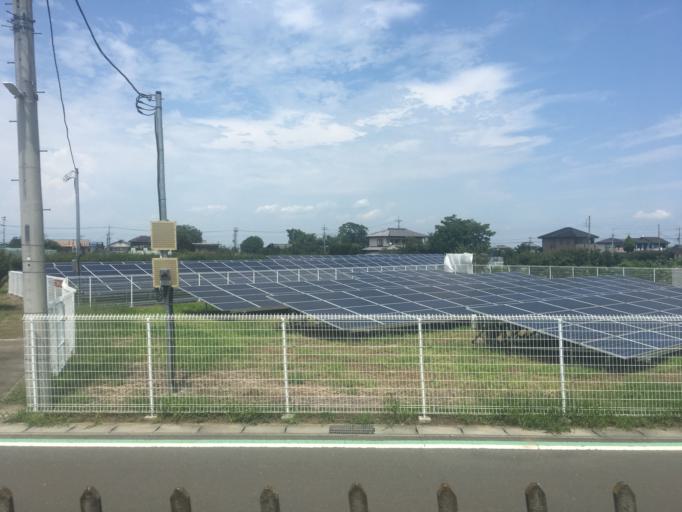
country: JP
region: Saitama
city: Kodamacho-kodamaminami
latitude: 36.2154
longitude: 139.1044
